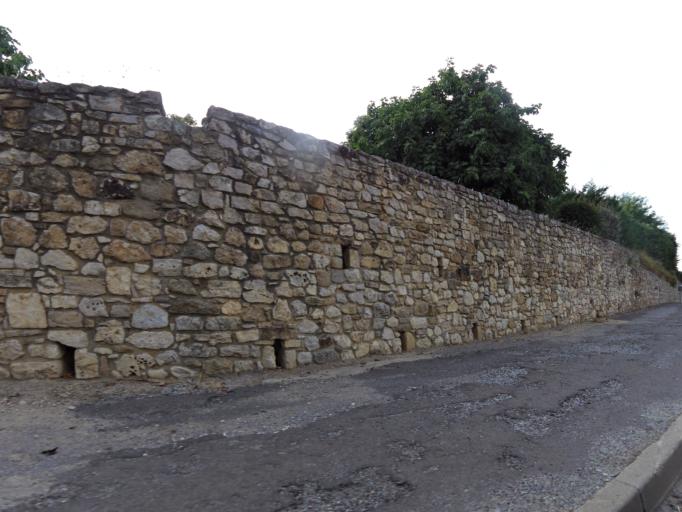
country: FR
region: Languedoc-Roussillon
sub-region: Departement du Gard
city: Saint-Genies-de-Malgoires
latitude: 43.9603
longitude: 4.2122
